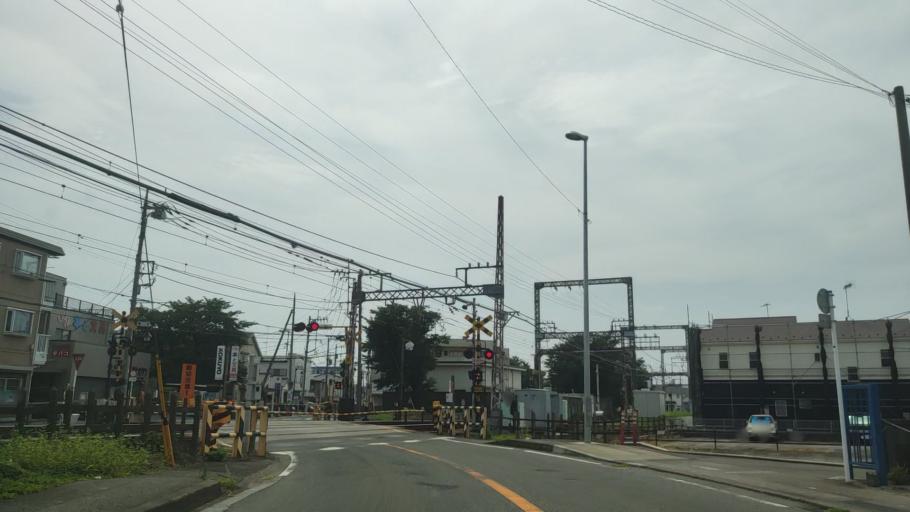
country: JP
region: Kanagawa
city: Zama
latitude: 35.4618
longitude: 139.3983
